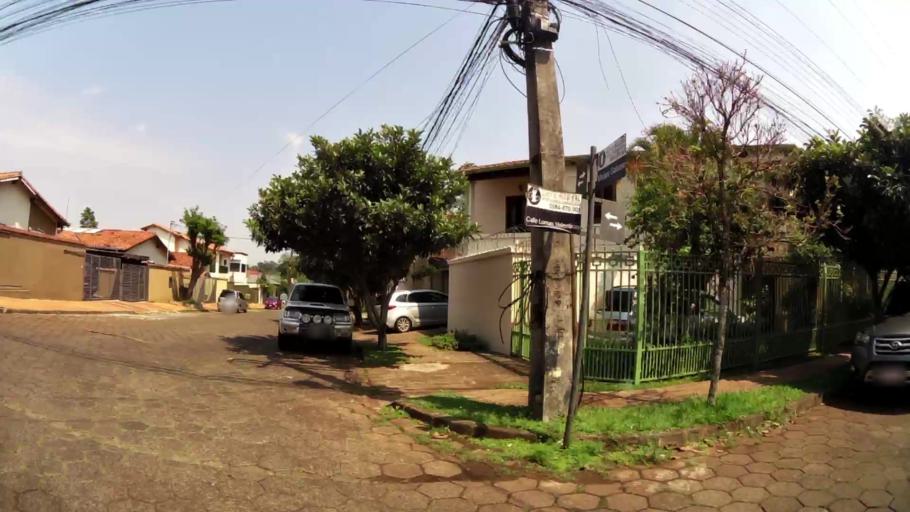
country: PY
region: Alto Parana
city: Presidente Franco
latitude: -25.5227
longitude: -54.6201
